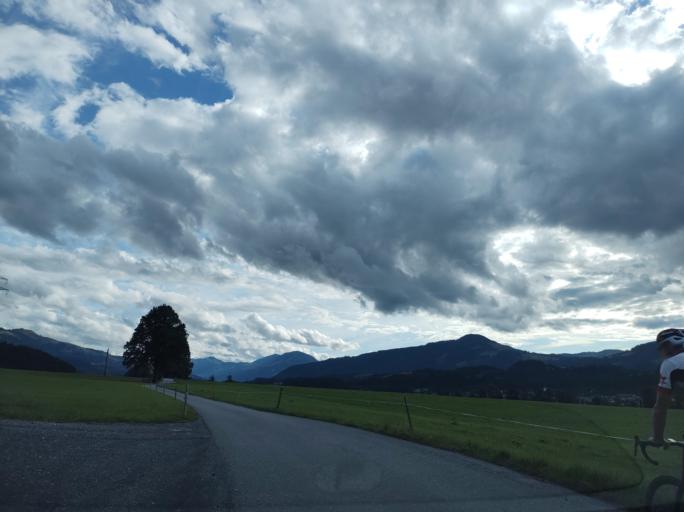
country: AT
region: Tyrol
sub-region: Politischer Bezirk Kitzbuhel
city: Oberndorf in Tirol
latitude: 47.5027
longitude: 12.3991
